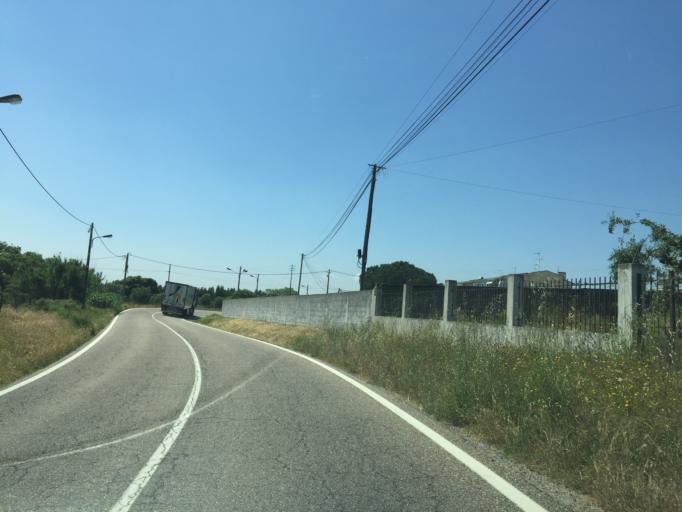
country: PT
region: Santarem
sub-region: Constancia
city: Constancia
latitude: 39.4819
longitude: -8.3010
